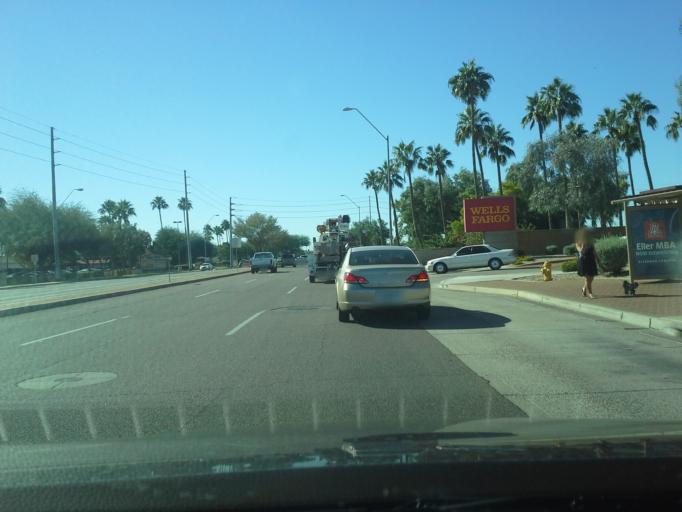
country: US
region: Arizona
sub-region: Maricopa County
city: Paradise Valley
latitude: 33.6407
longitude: -111.9778
